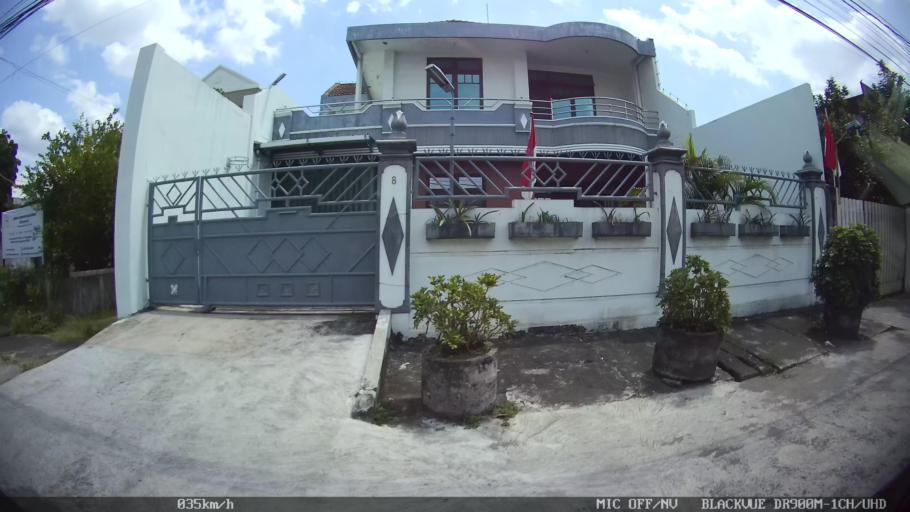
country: ID
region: Daerah Istimewa Yogyakarta
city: Gamping Lor
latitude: -7.8013
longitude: 110.3419
